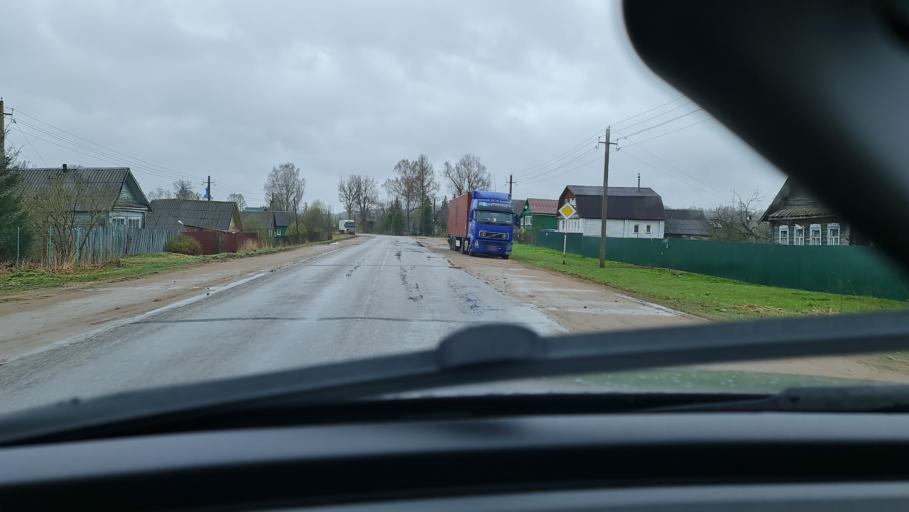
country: RU
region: Novgorod
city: Valday
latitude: 58.0352
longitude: 32.9628
